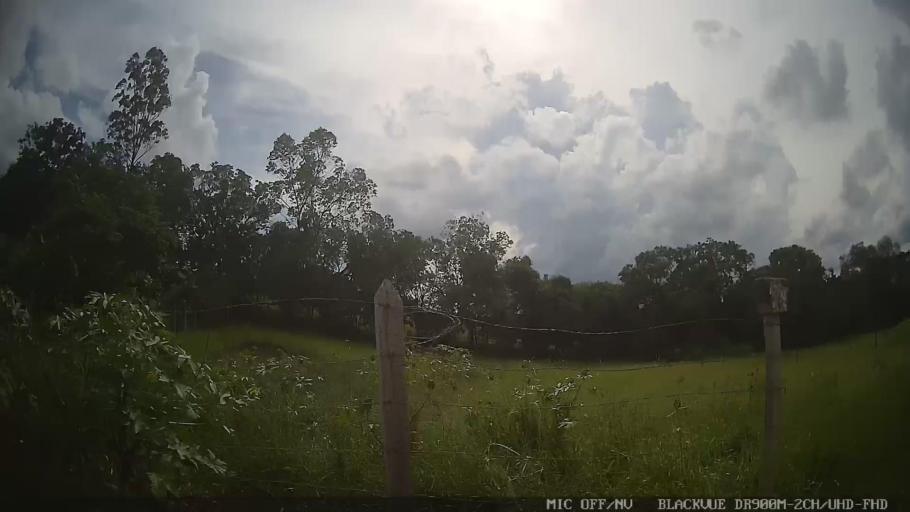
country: BR
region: Minas Gerais
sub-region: Extrema
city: Extrema
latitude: -22.8336
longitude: -46.2788
